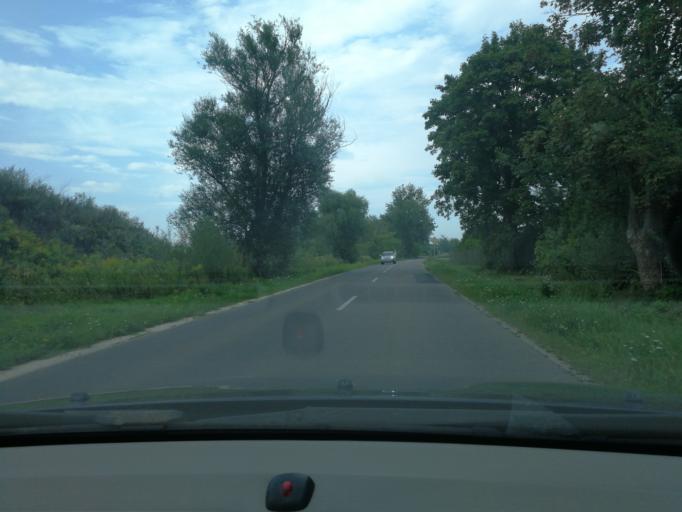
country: PL
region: Masovian Voivodeship
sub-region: Powiat grodziski
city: Grodzisk Mazowiecki
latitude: 52.1415
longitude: 20.6309
